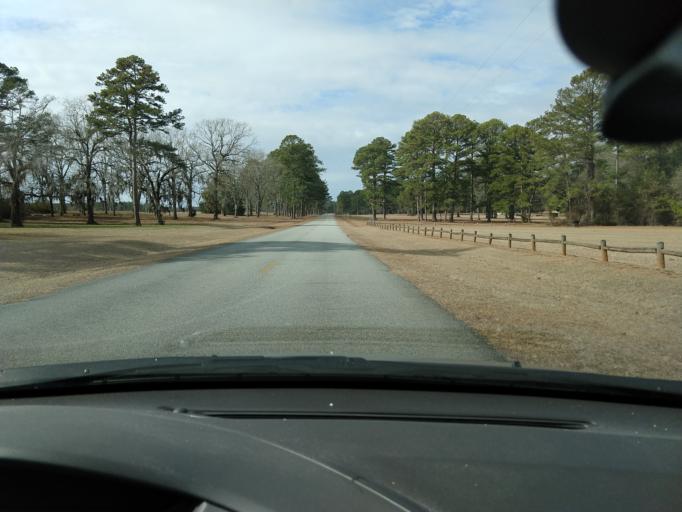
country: US
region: Georgia
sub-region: Early County
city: Blakely
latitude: 31.4669
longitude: -84.9452
